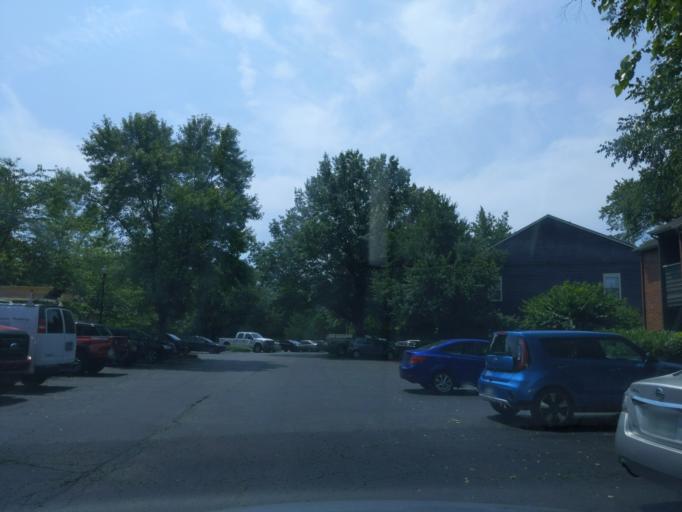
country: US
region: Tennessee
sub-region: Williamson County
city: Brentwood Estates
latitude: 36.0432
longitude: -86.7397
